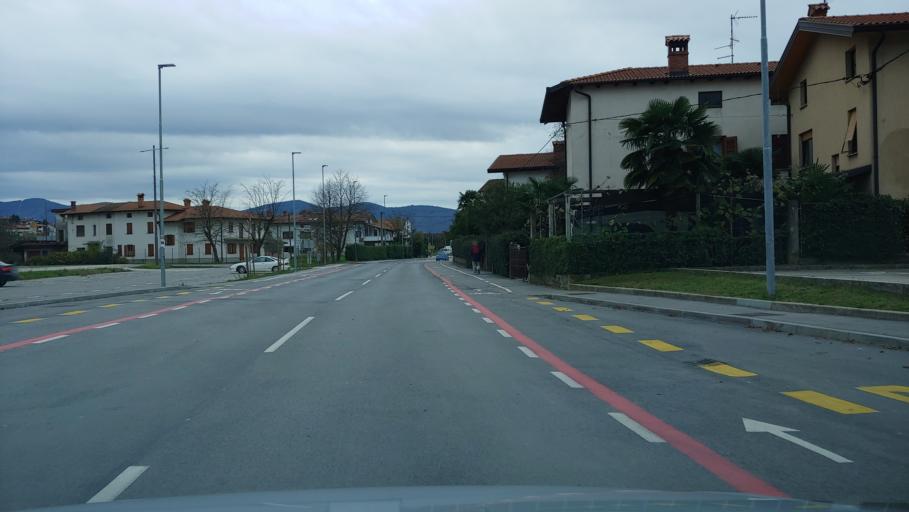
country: SI
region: Sempeter-Vrtojba
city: Sempeter pri Gorici
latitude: 45.9242
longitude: 13.6407
